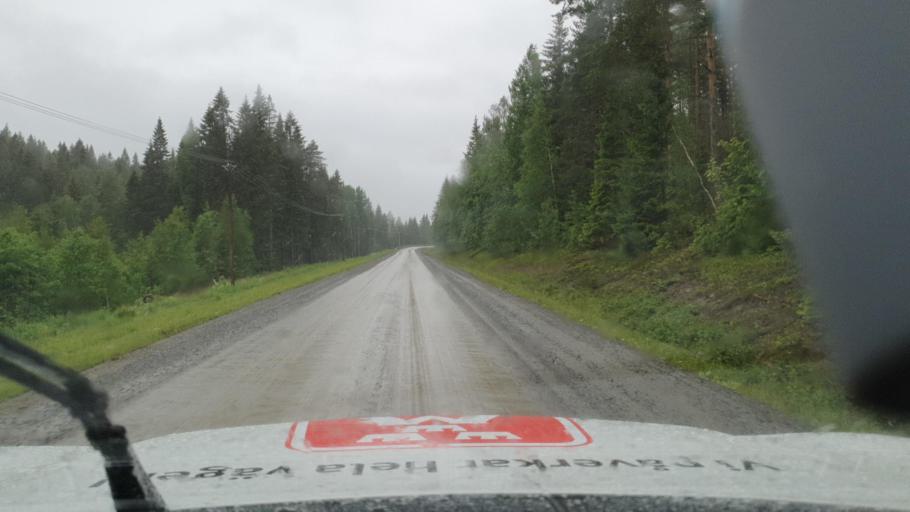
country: SE
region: Vaesterbotten
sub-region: Bjurholms Kommun
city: Bjurholm
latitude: 63.9171
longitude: 19.3816
